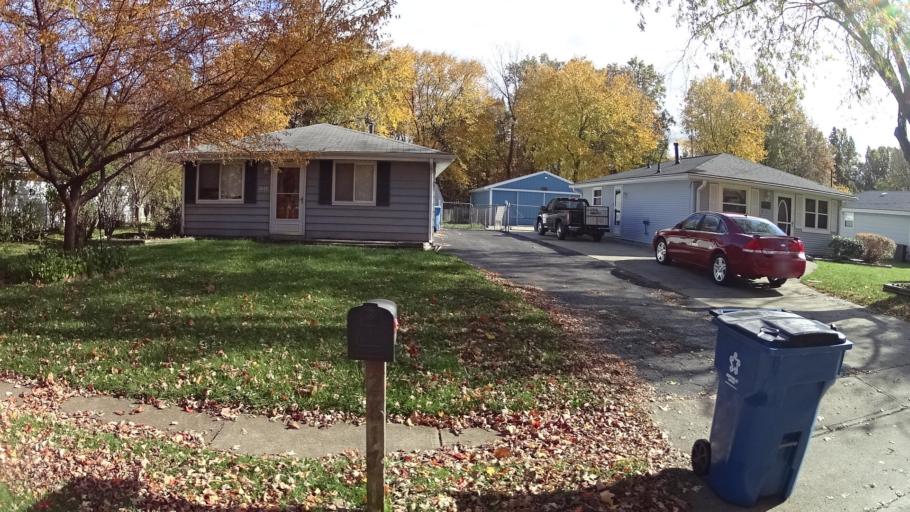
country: US
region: Ohio
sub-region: Lorain County
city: Lorain
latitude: 41.4444
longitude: -82.2269
